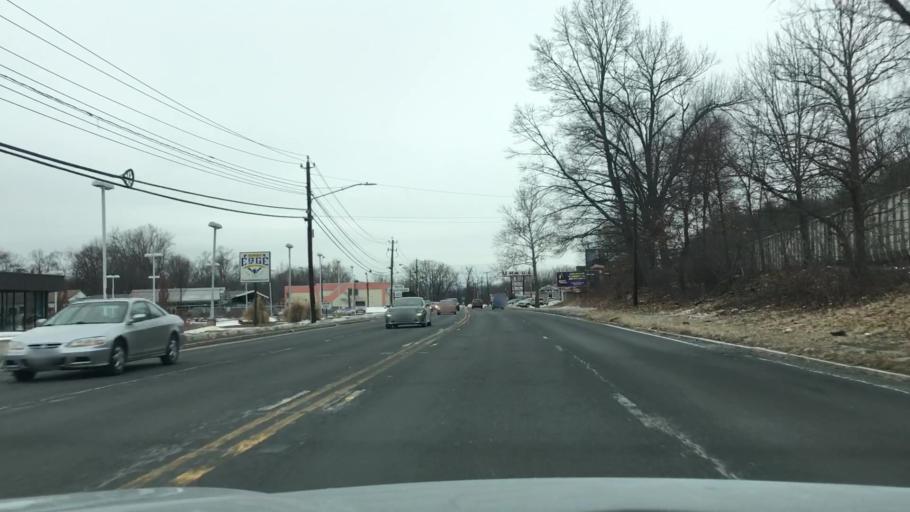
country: US
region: Massachusetts
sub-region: Hampden County
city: Westfield
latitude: 42.1102
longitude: -72.7091
